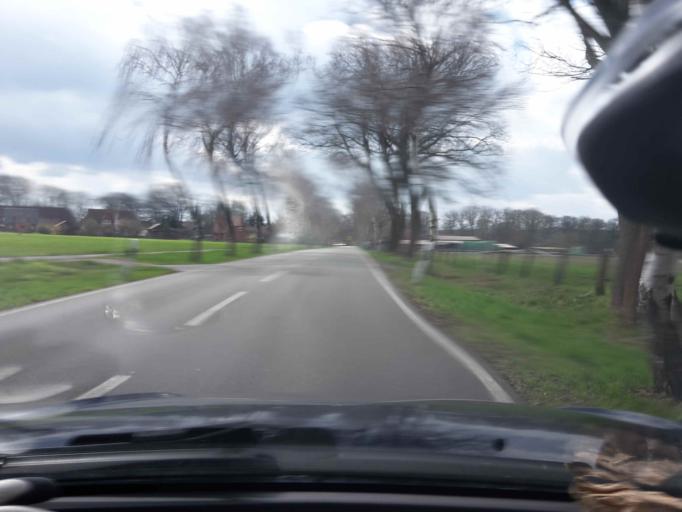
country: DE
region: Lower Saxony
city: Hanstedt
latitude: 53.2406
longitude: 10.0277
